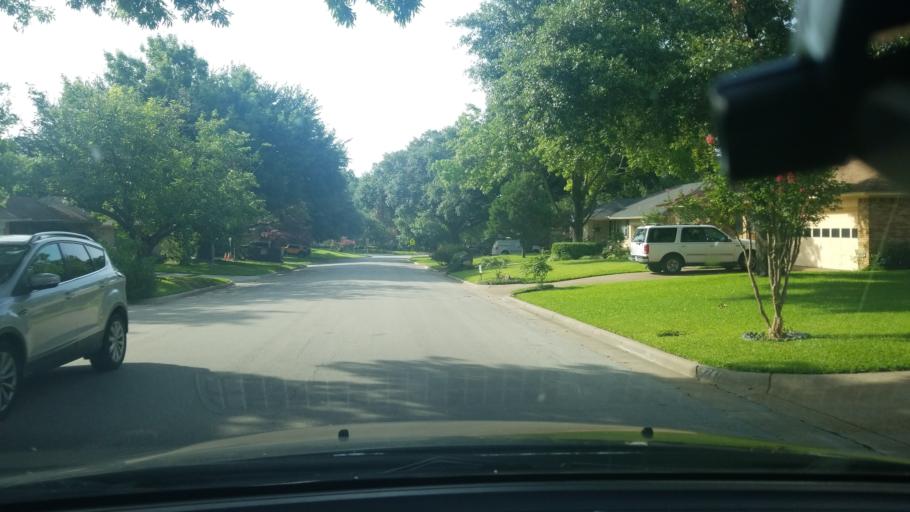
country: US
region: Texas
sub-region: Dallas County
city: Highland Park
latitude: 32.8035
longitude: -96.7096
